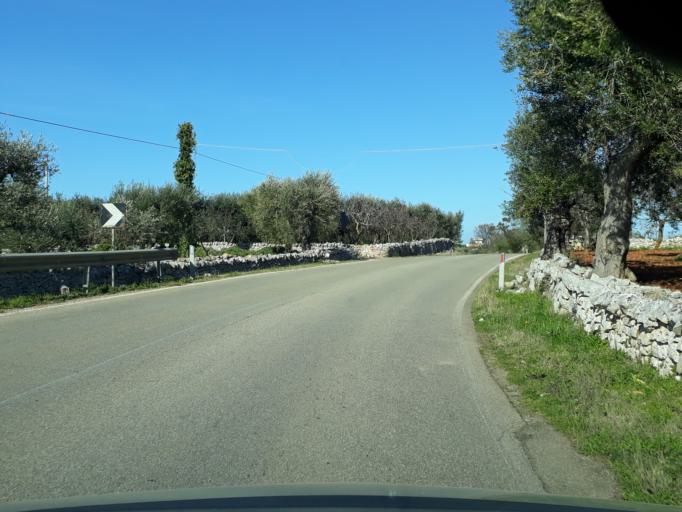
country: IT
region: Apulia
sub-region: Provincia di Bari
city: Cozzana
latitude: 40.8684
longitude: 17.2606
